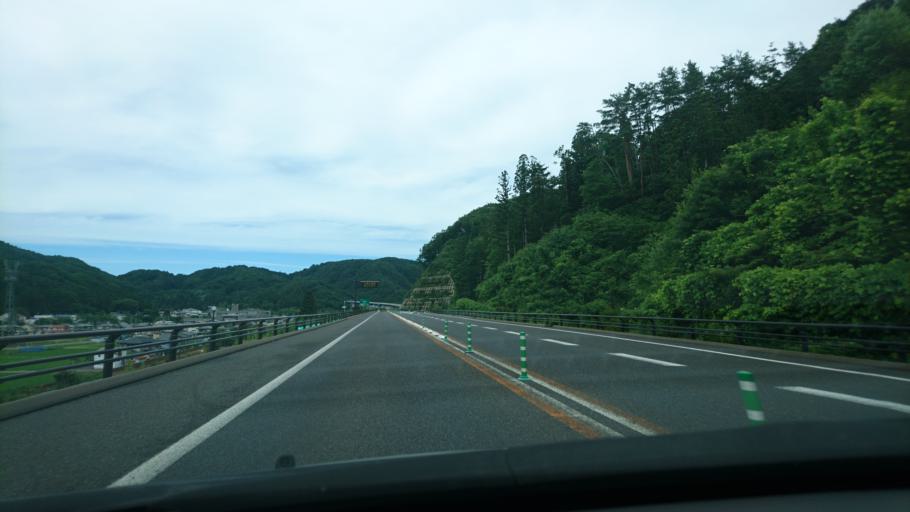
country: JP
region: Iwate
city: Miyako
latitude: 39.9984
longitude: 141.8854
